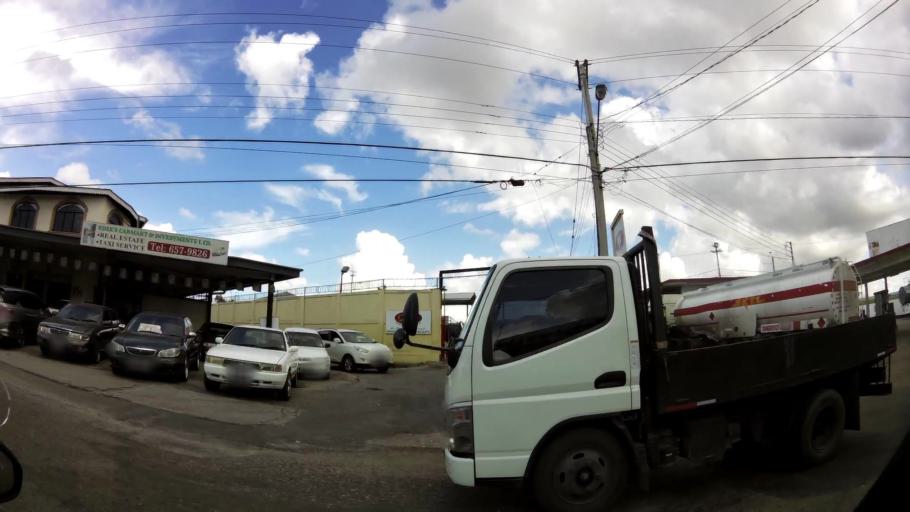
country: TT
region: City of San Fernando
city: Mon Repos
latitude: 10.2635
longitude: -61.4588
